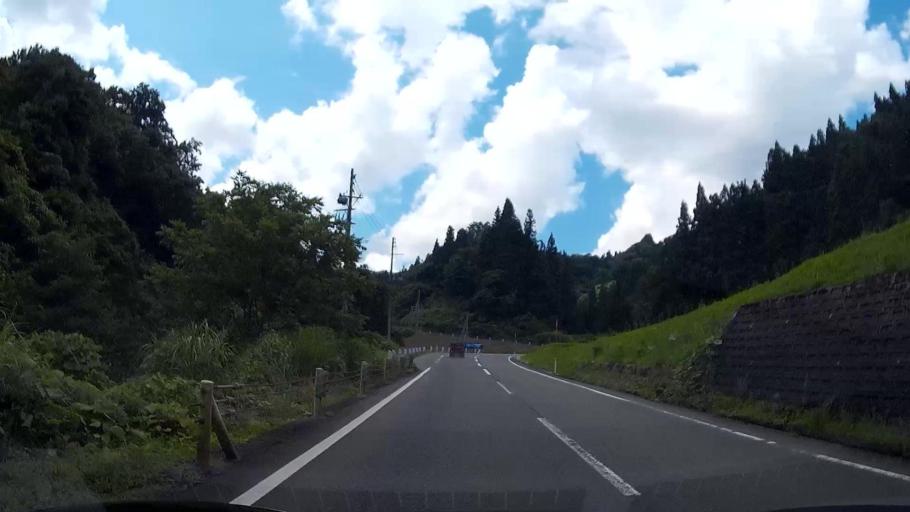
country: JP
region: Niigata
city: Shiozawa
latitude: 37.0216
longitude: 138.8129
